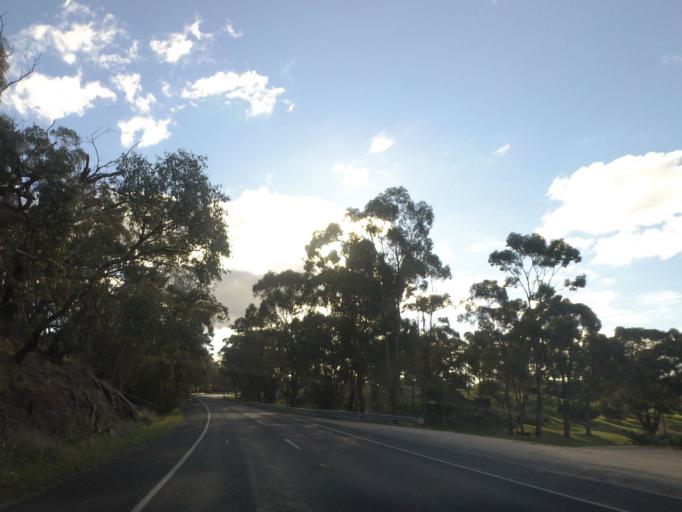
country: AU
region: Victoria
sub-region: Mount Alexander
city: Castlemaine
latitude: -37.0889
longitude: 144.2825
